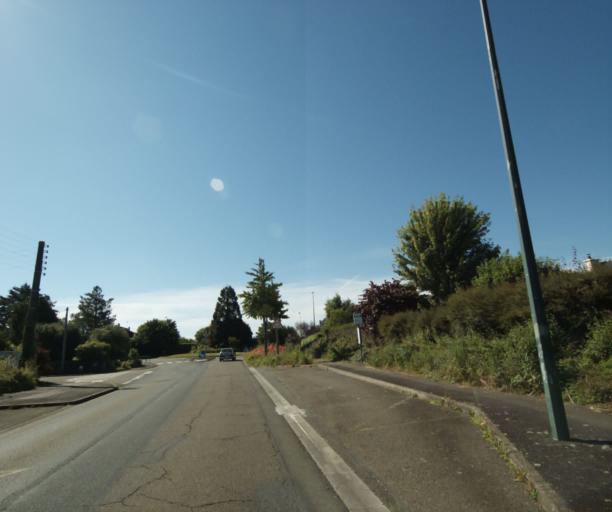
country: FR
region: Pays de la Loire
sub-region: Departement de la Mayenne
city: Laval
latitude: 48.0552
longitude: -0.7504
